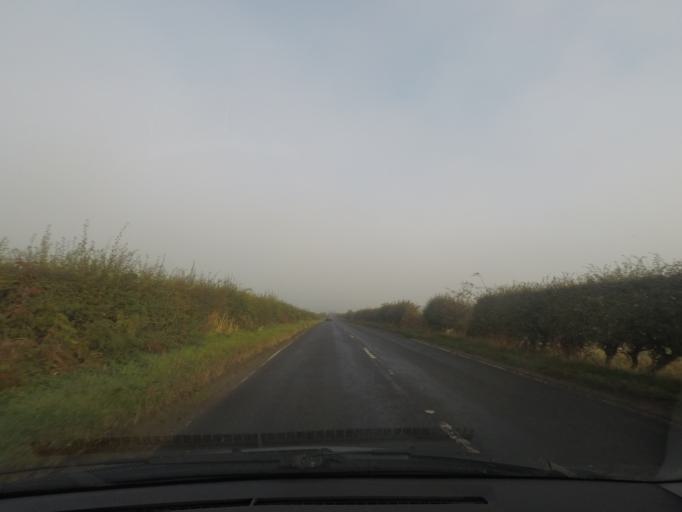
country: GB
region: England
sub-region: City and Borough of Leeds
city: Walton
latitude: 54.0098
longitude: -1.3076
